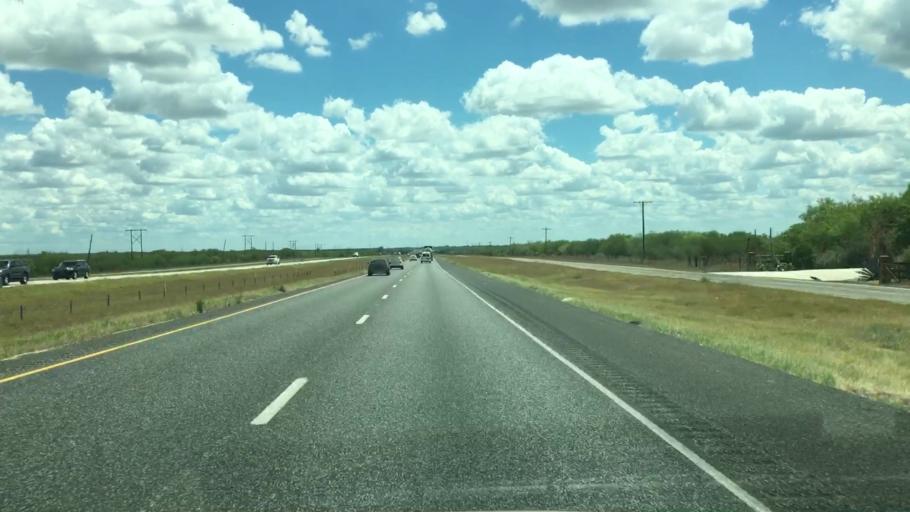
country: US
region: Texas
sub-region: Atascosa County
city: Pleasanton
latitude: 28.8641
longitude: -98.3897
